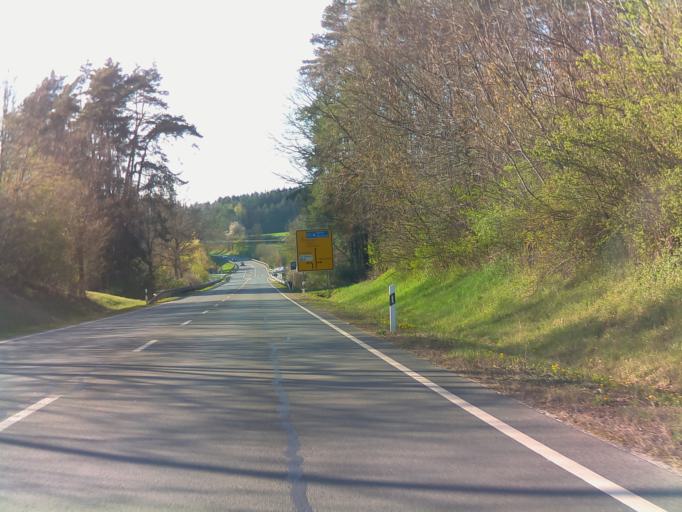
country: DE
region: Bavaria
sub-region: Upper Palatinate
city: Auerbach
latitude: 49.7025
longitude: 11.5749
